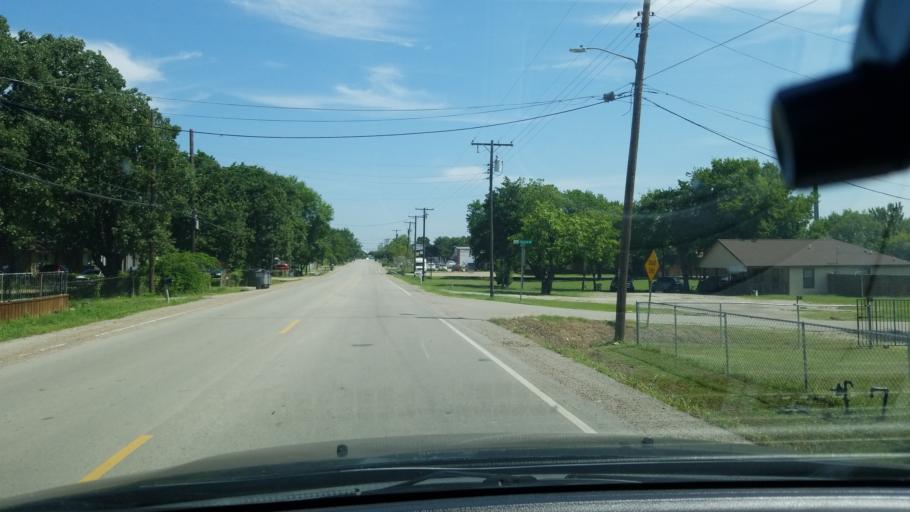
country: US
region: Texas
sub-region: Dallas County
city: Balch Springs
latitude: 32.7275
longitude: -96.6313
